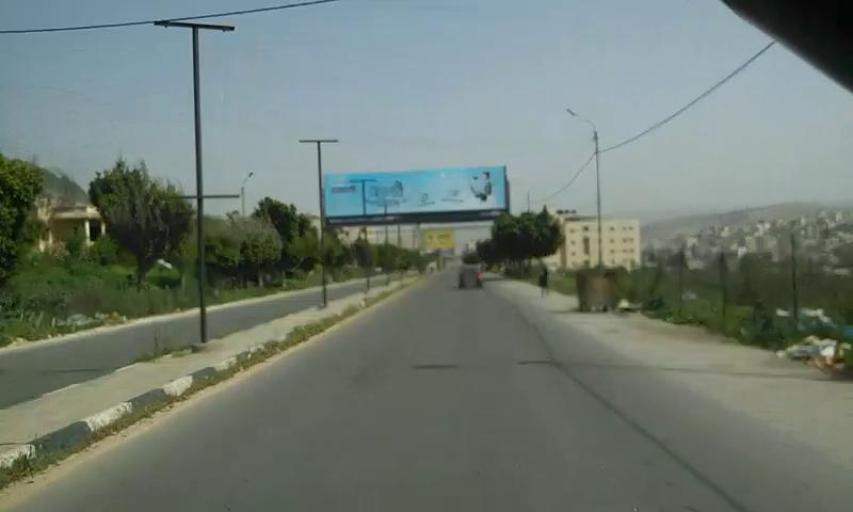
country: PS
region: West Bank
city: Kafr Qallil
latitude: 32.1869
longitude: 35.2804
